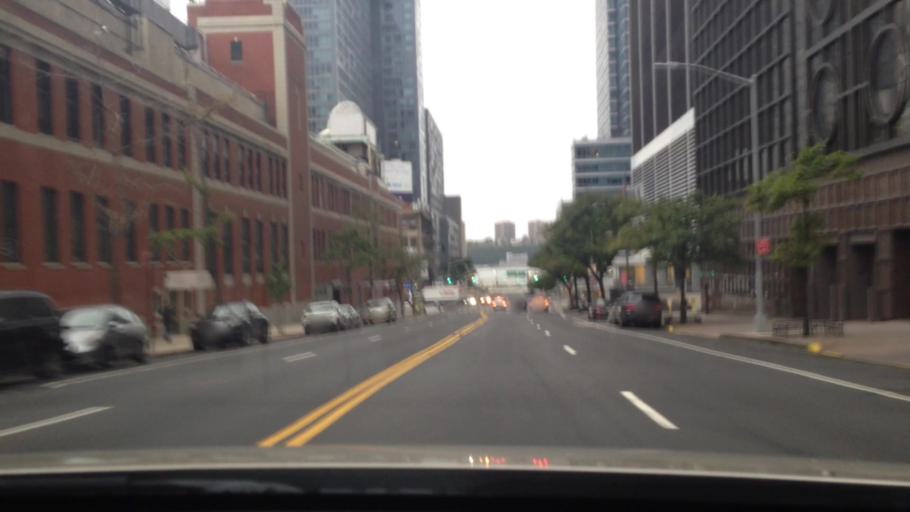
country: US
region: New Jersey
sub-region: Hudson County
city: Guttenberg
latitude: 40.7695
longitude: -73.9896
